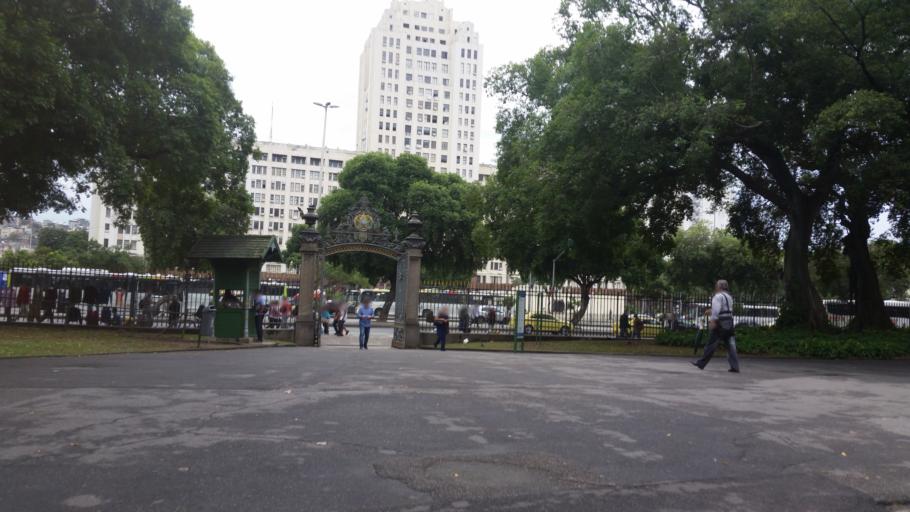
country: BR
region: Rio de Janeiro
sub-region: Rio De Janeiro
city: Rio de Janeiro
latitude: -22.9052
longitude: -43.1893
